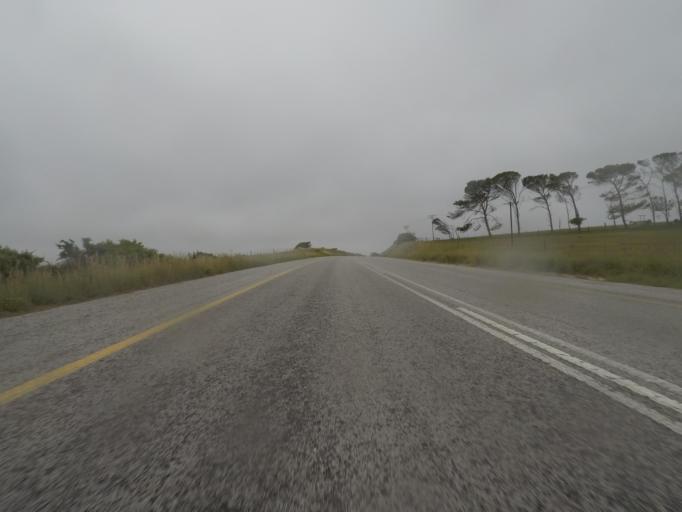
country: ZA
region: Eastern Cape
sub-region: Cacadu District Municipality
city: Grahamstown
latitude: -33.6438
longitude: 26.3481
